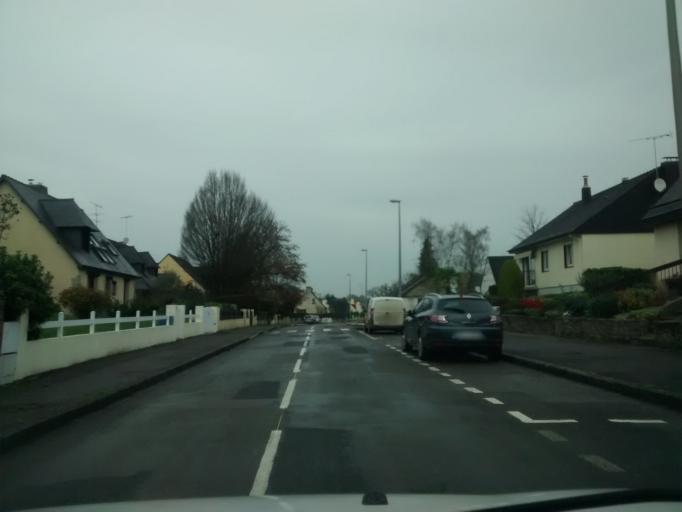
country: FR
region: Brittany
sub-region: Departement d'Ille-et-Vilaine
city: Acigne
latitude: 48.1311
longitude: -1.5440
